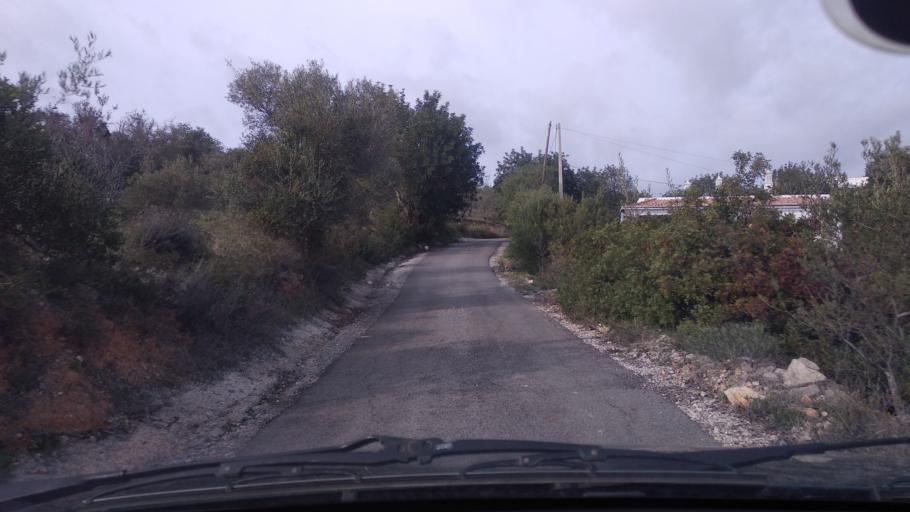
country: PT
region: Faro
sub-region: Sao Bras de Alportel
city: Sao Bras de Alportel
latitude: 37.1167
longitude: -7.9095
